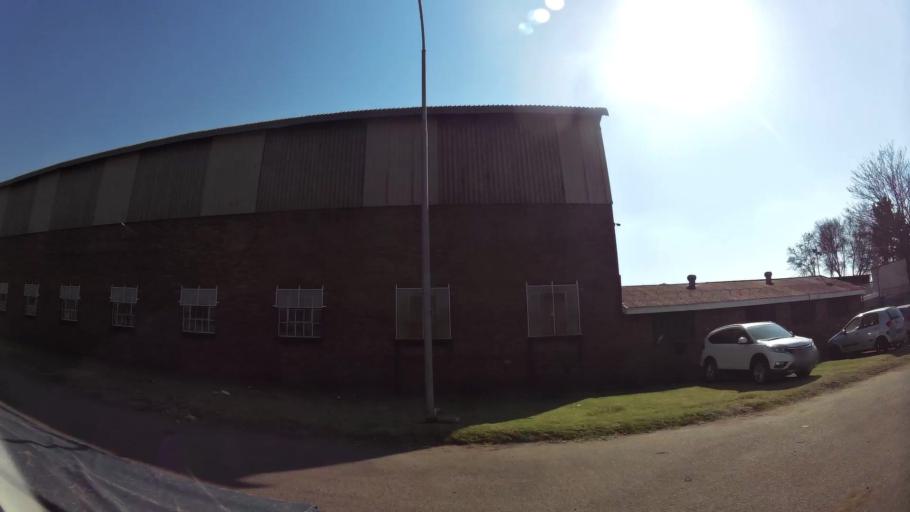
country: ZA
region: Gauteng
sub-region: Ekurhuleni Metropolitan Municipality
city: Benoni
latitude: -26.2035
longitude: 28.3073
